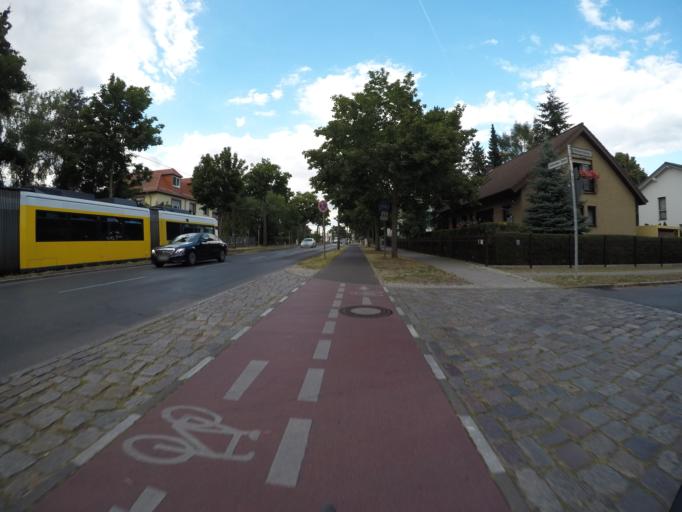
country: DE
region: Berlin
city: Mahlsdorf
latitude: 52.4844
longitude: 13.6030
